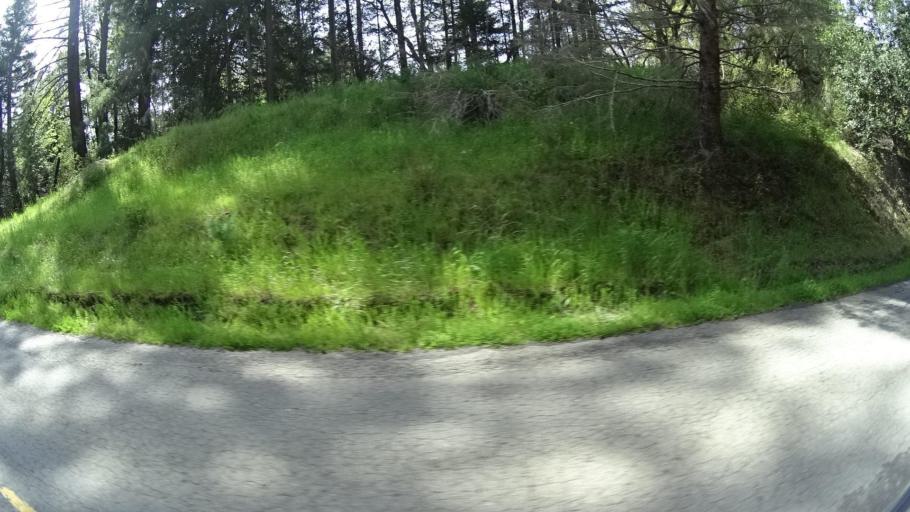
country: US
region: California
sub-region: Humboldt County
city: Redway
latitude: 40.4310
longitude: -123.7656
